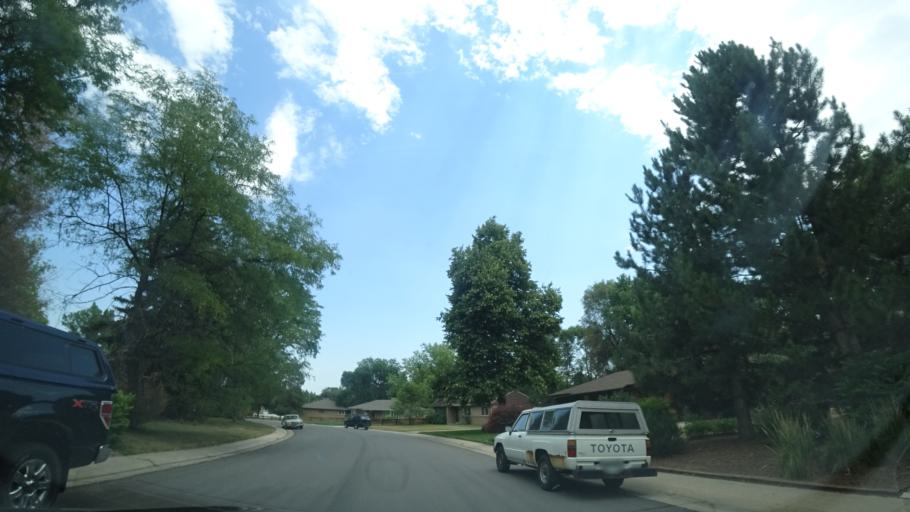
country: US
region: Colorado
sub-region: Jefferson County
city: Lakewood
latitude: 39.7216
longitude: -105.0955
